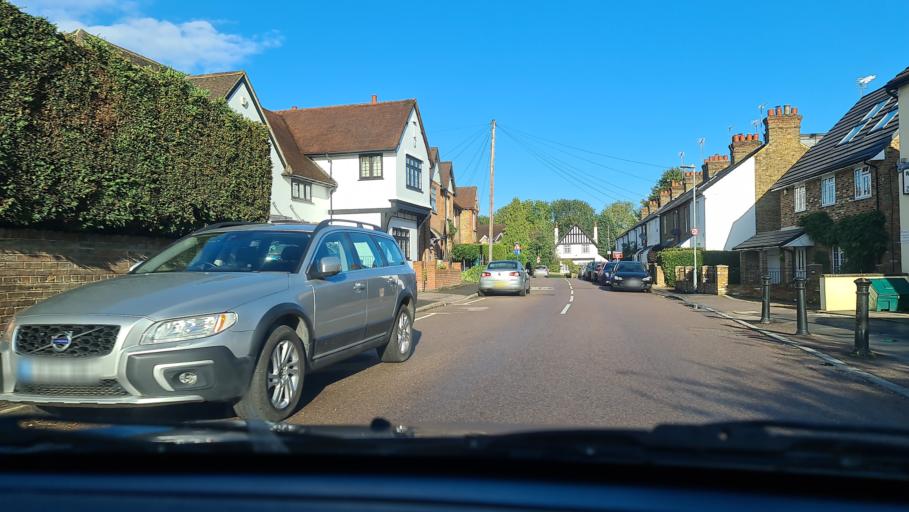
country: GB
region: England
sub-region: Buckinghamshire
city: Chalfont St Giles
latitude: 51.6462
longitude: -0.5279
